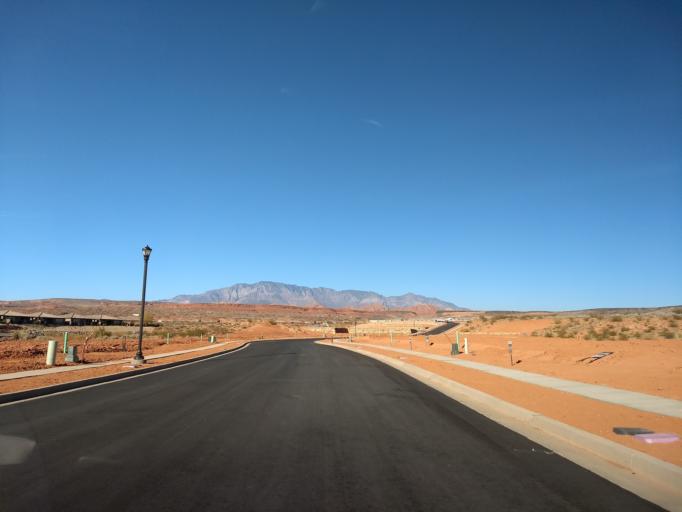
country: US
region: Utah
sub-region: Washington County
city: Washington
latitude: 37.1382
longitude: -113.4807
